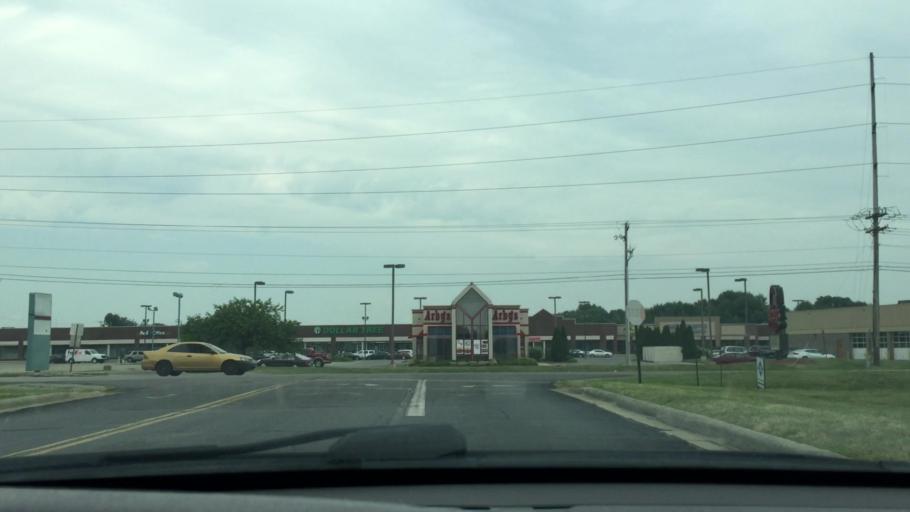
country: US
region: Ohio
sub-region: Franklin County
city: Reynoldsburg
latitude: 39.9260
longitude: -82.8319
